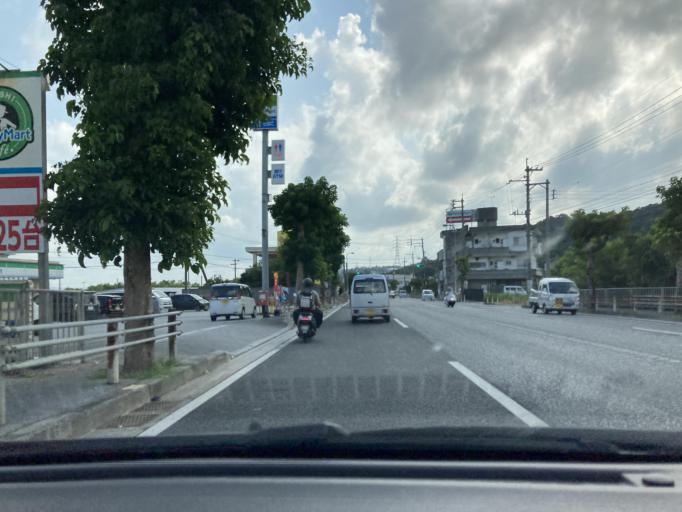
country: JP
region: Okinawa
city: Ginowan
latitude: 26.2624
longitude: 127.7885
